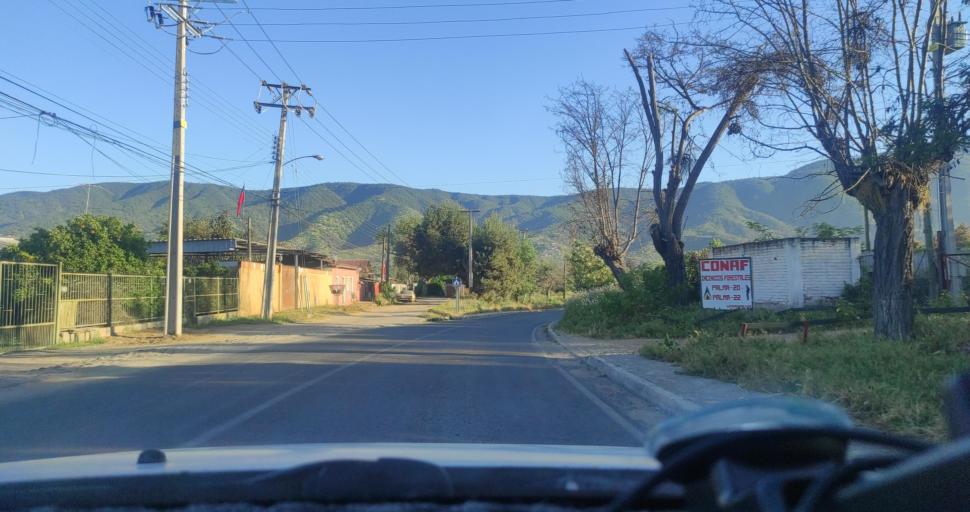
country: CL
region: Valparaiso
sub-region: Provincia de Marga Marga
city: Limache
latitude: -33.0024
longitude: -71.2240
